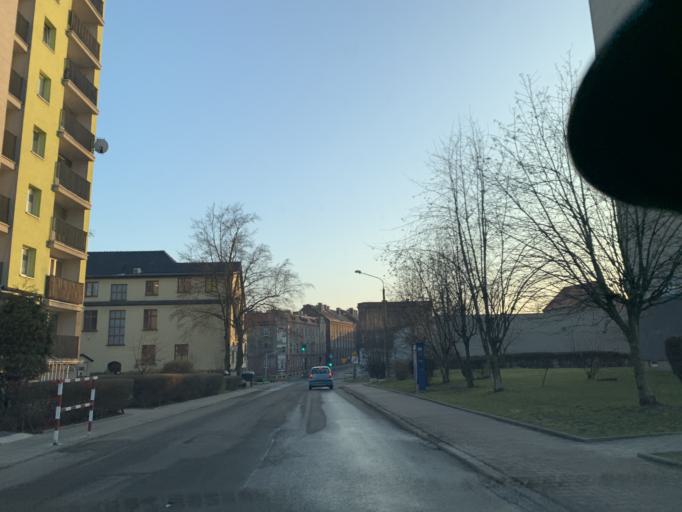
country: PL
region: Silesian Voivodeship
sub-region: Bytom
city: Bytom
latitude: 50.3387
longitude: 18.8916
